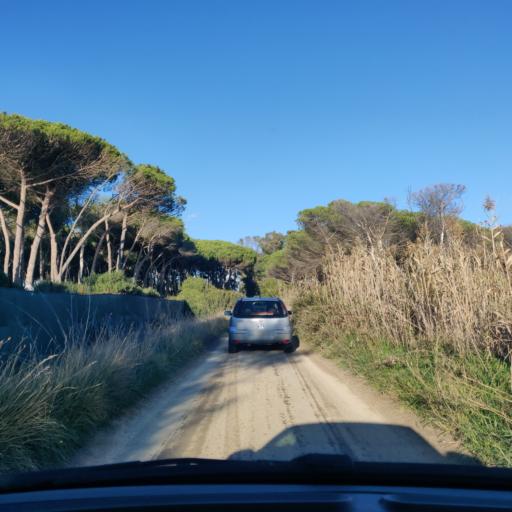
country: IT
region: Latium
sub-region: Citta metropolitana di Roma Capitale
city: Aurelia
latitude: 42.1484
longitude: 11.7444
